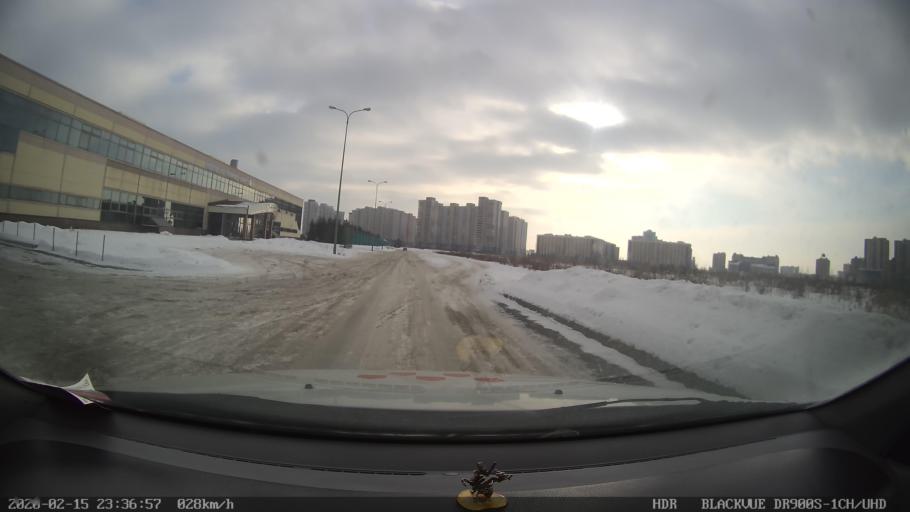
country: RU
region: Tatarstan
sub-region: Gorod Kazan'
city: Kazan
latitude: 55.7906
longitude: 49.1930
